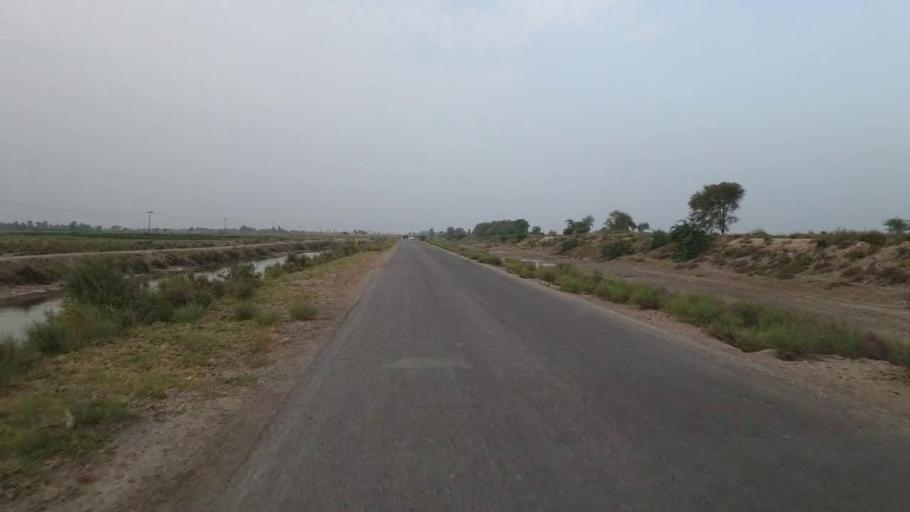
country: PK
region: Sindh
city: Daur
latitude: 26.4428
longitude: 68.2796
